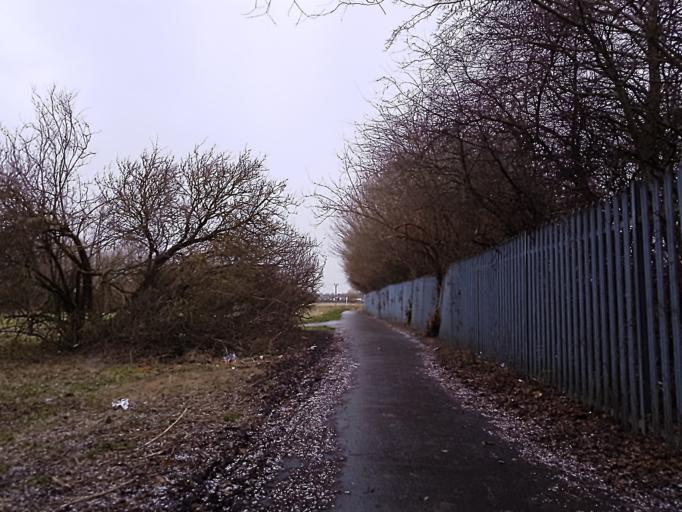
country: GB
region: England
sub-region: North East Lincolnshire
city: Great Coates
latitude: 53.5656
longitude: -0.1199
